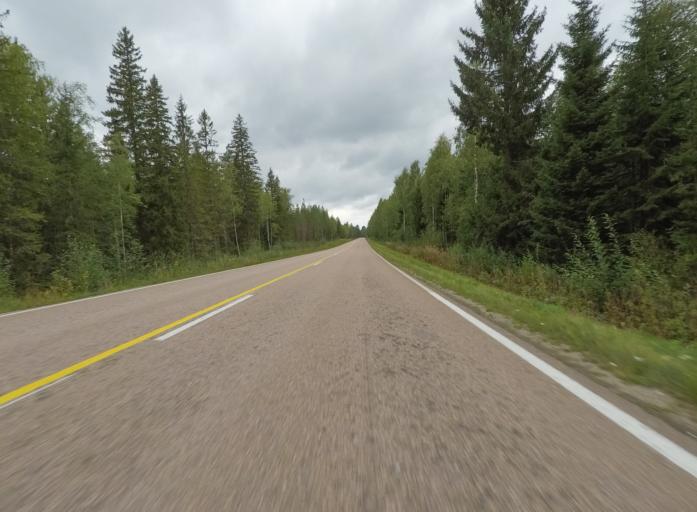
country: FI
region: Central Finland
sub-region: Jyvaeskylae
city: Hankasalmi
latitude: 62.3586
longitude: 26.5556
